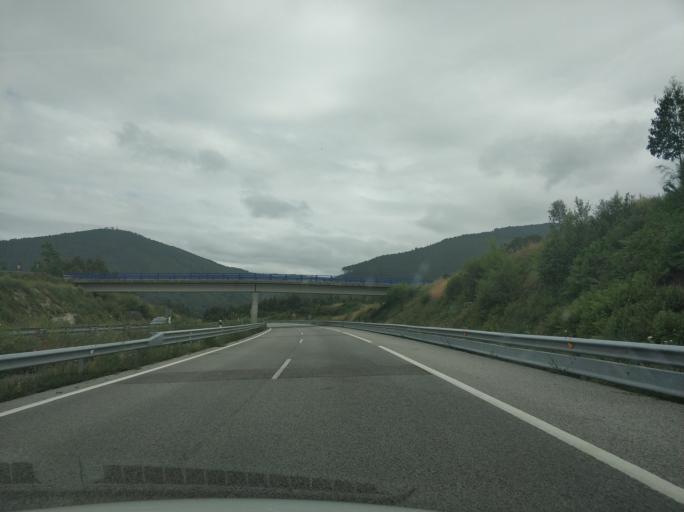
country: ES
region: Asturias
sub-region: Province of Asturias
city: Cudillero
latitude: 43.5582
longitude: -6.2072
